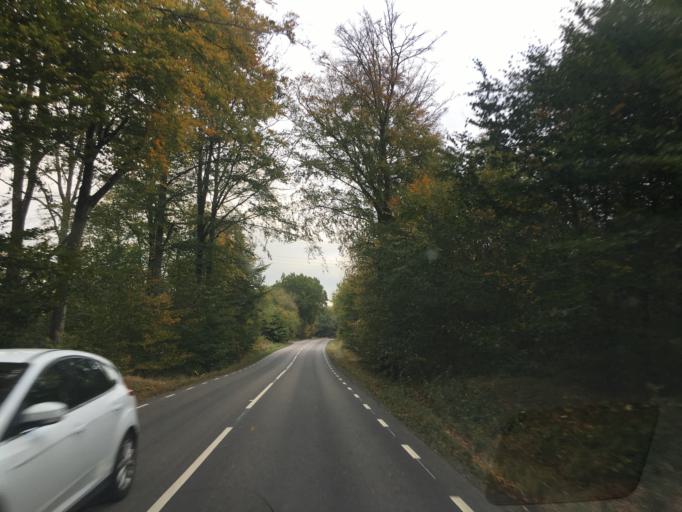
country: SE
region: Skane
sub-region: Simrishamns Kommun
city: Kivik
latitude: 55.6337
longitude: 14.1102
